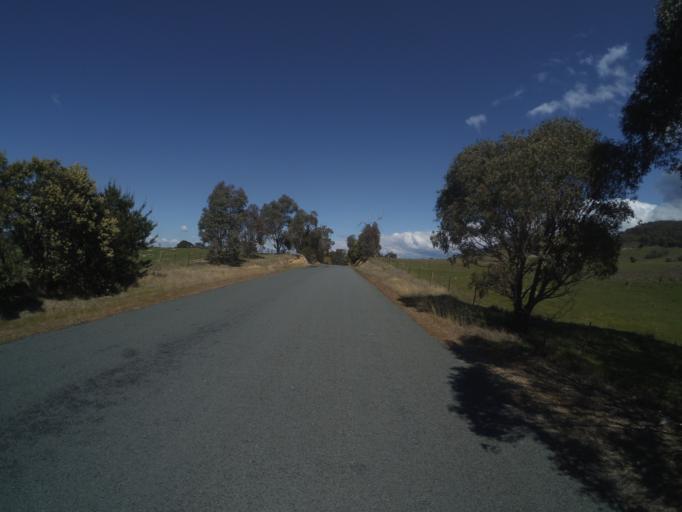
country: AU
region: Australian Capital Territory
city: Macquarie
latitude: -35.2251
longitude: 148.9124
